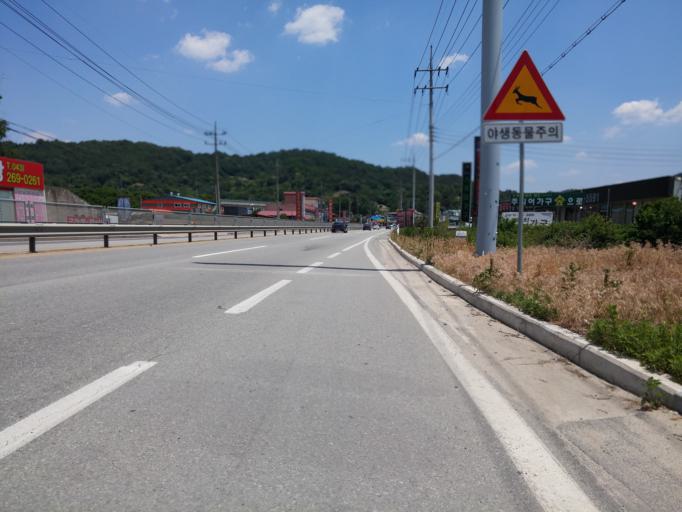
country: KR
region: Chungcheongbuk-do
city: Cheongju-si
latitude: 36.5614
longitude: 127.4368
